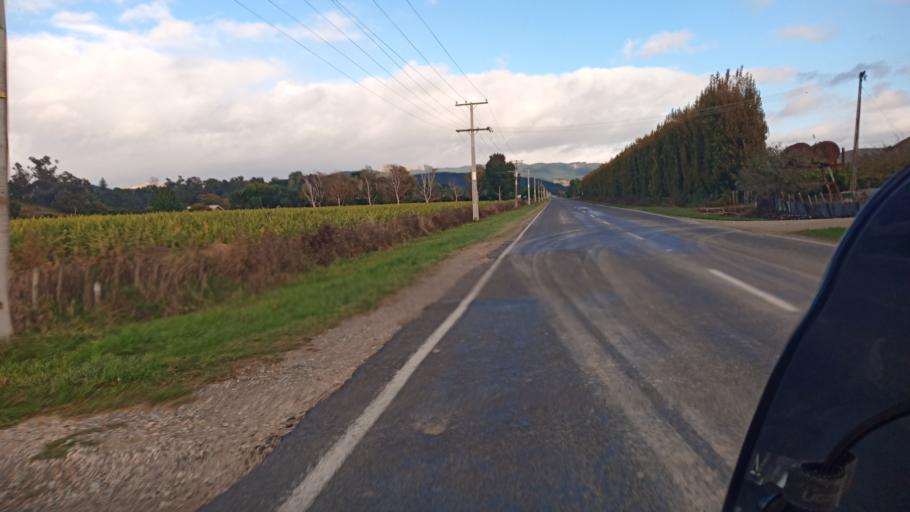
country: NZ
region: Gisborne
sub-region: Gisborne District
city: Gisborne
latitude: -38.6312
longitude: 177.8873
